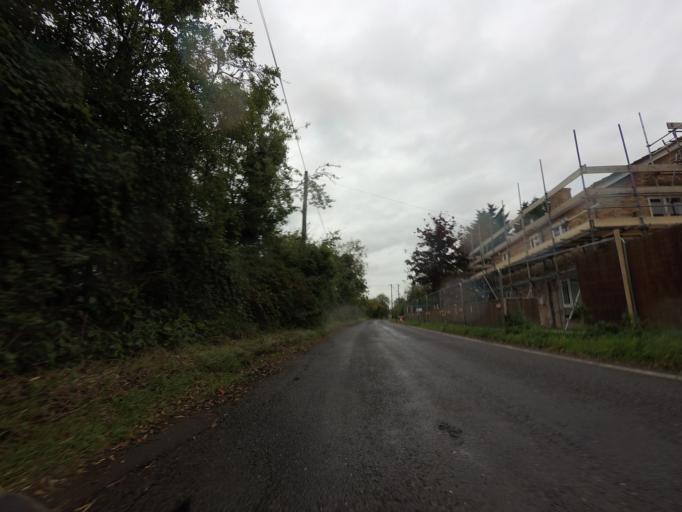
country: GB
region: England
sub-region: Cambridgeshire
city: Comberton
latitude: 52.1656
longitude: -0.0117
